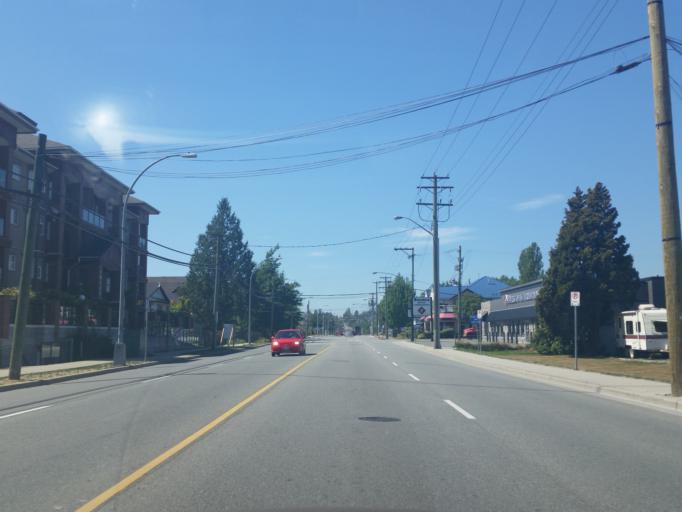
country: CA
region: British Columbia
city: Langley
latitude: 49.1044
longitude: -122.6750
